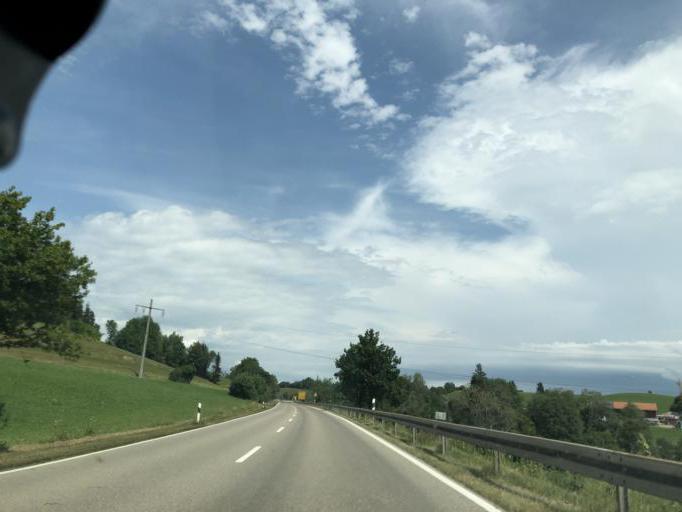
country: DE
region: Bavaria
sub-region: Swabia
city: Oy-Mittelberg
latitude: 47.6291
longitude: 10.4537
